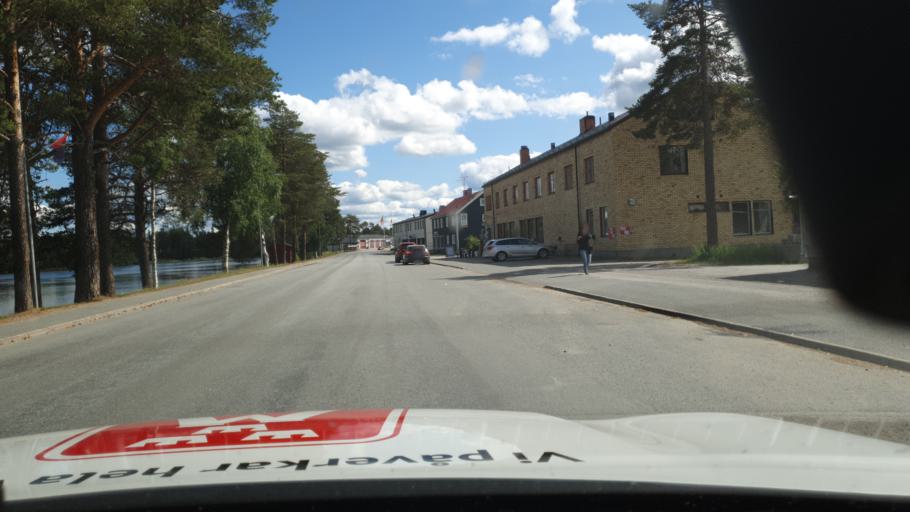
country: SE
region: Vaesterbotten
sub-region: Sorsele Kommun
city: Sorsele
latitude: 65.5383
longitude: 17.5255
